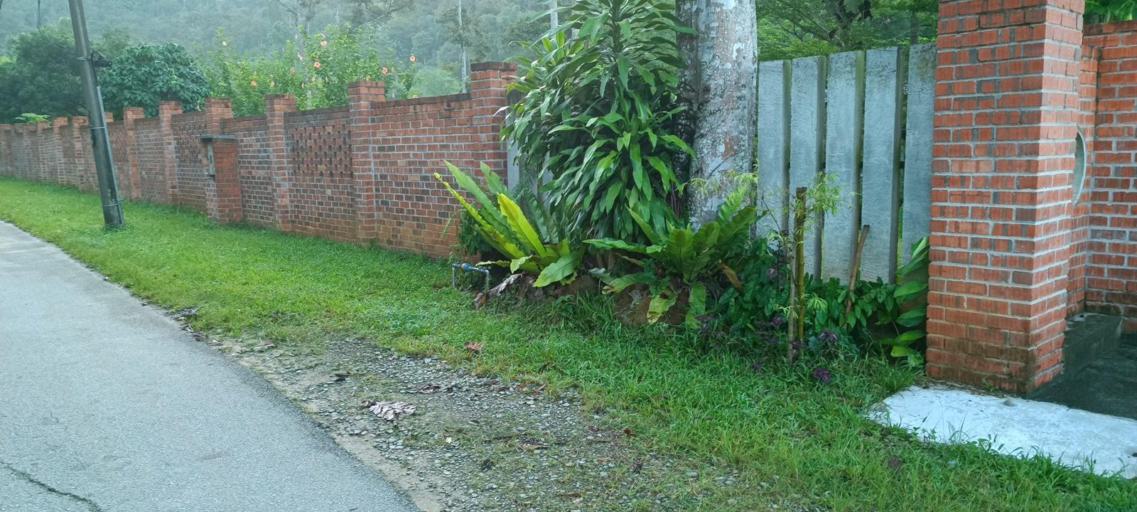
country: MY
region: Penang
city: Bukit Mertajam
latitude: 5.3550
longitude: 100.4940
